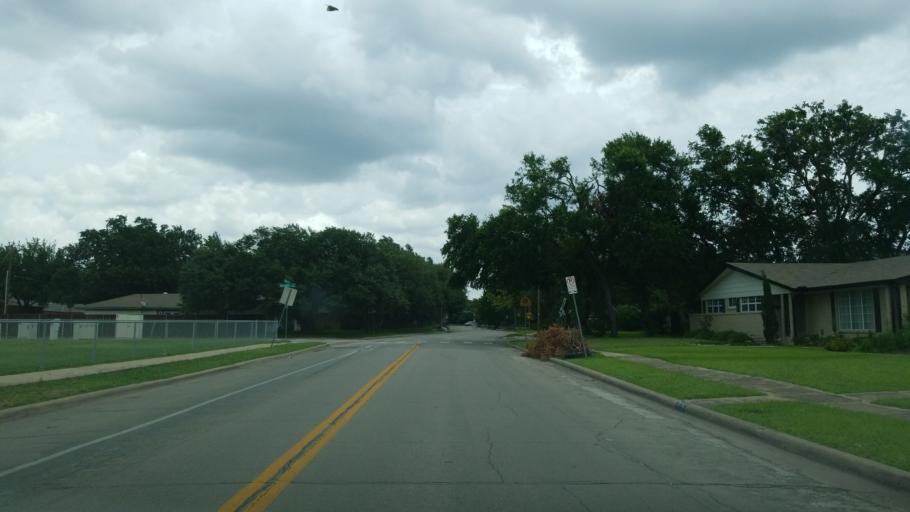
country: US
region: Texas
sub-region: Dallas County
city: Farmers Branch
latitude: 32.8879
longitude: -96.8735
